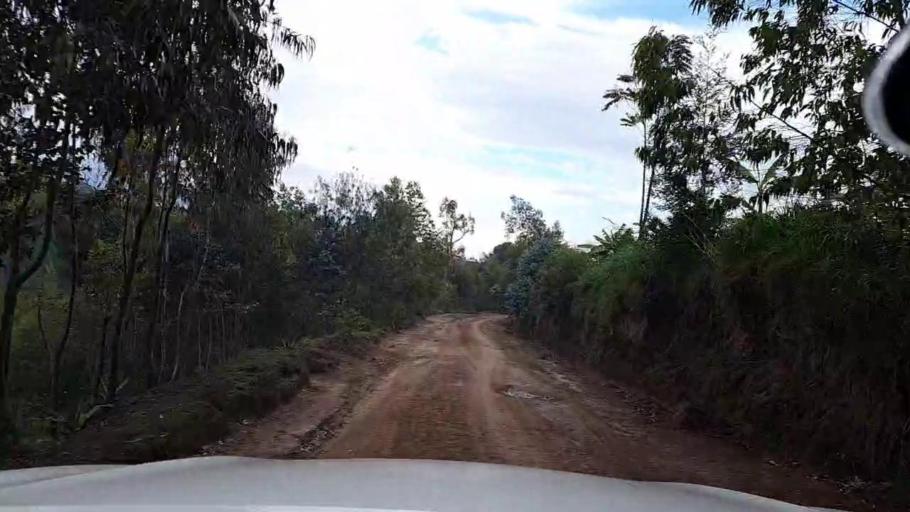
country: BI
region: Kayanza
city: Kayanza
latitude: -2.7986
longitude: 29.5018
